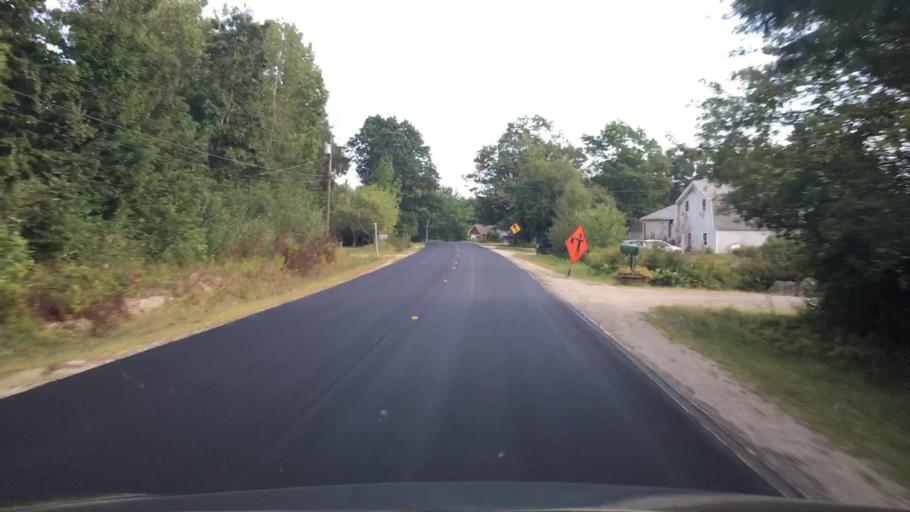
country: US
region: Maine
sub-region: Hancock County
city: Orland
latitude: 44.5473
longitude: -68.6205
